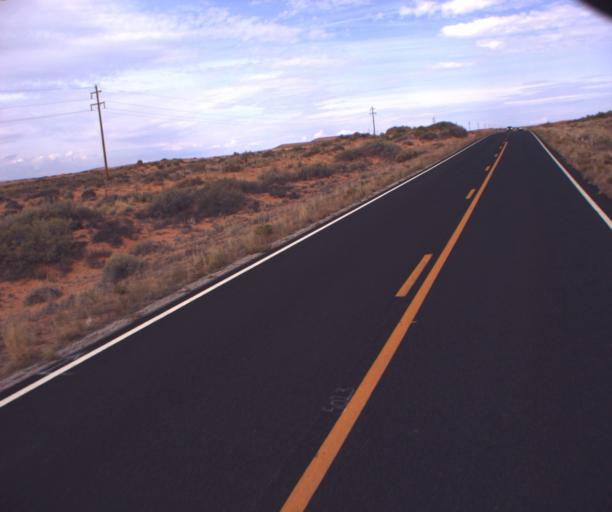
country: US
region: Arizona
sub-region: Apache County
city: Many Farms
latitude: 36.8120
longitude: -109.6468
